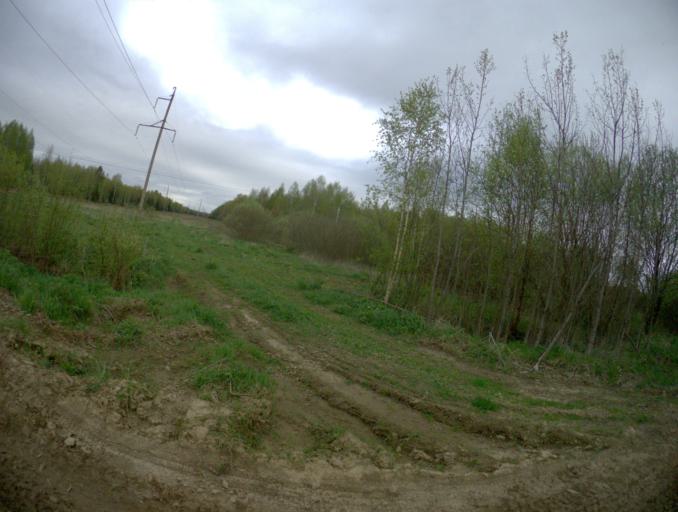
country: RU
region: Vladimir
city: Golovino
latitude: 55.9847
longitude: 40.4036
